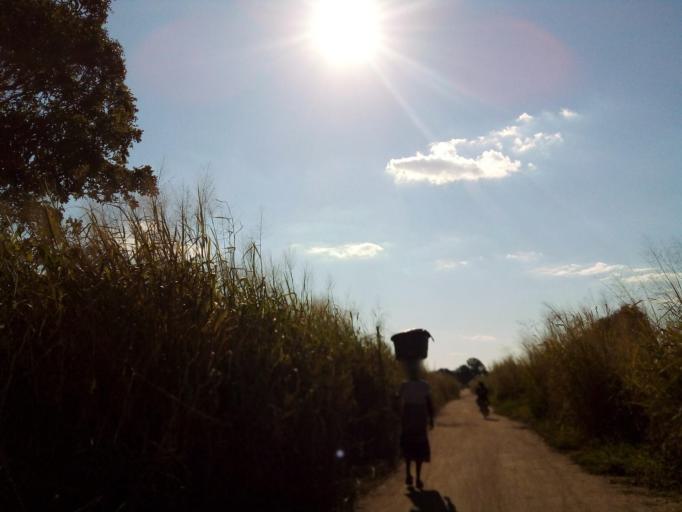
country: MZ
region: Zambezia
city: Quelimane
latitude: -17.5434
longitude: 36.6928
